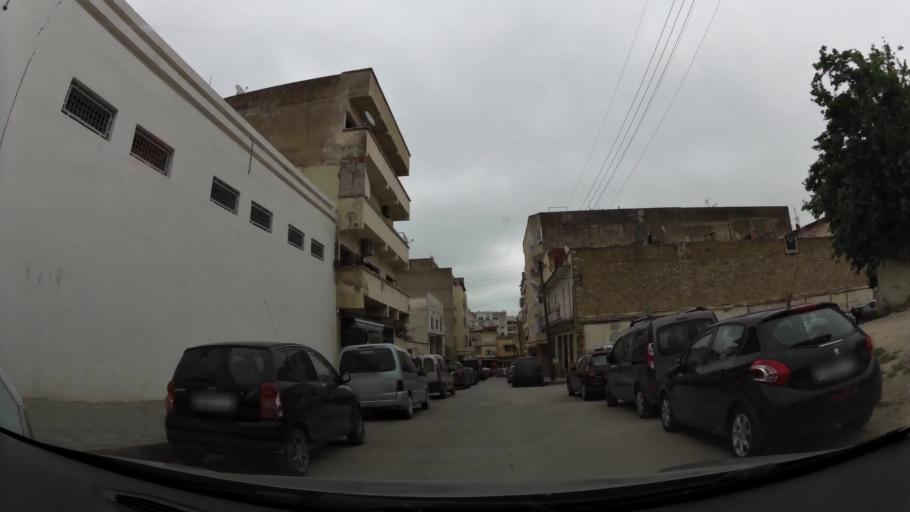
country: MA
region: Fes-Boulemane
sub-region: Fes
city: Fes
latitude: 34.0308
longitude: -4.9964
